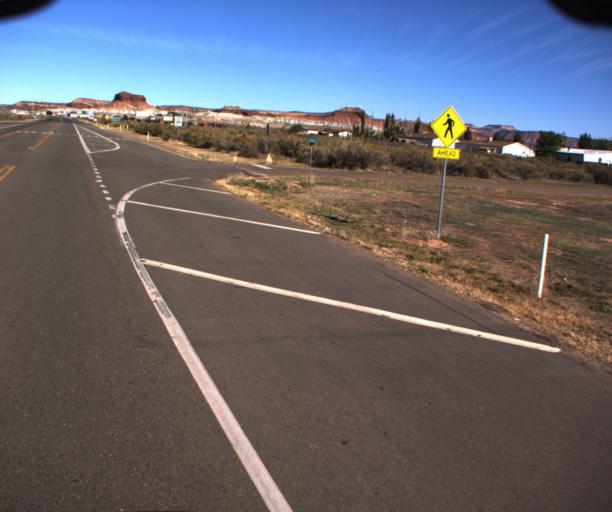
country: US
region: Arizona
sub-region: Coconino County
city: Fredonia
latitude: 36.9592
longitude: -112.5269
